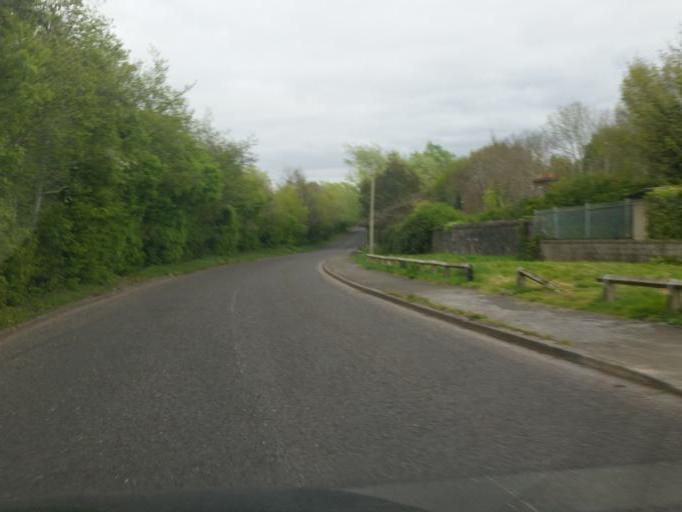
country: IE
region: Leinster
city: Castleknock
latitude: 53.3890
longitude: -6.3514
